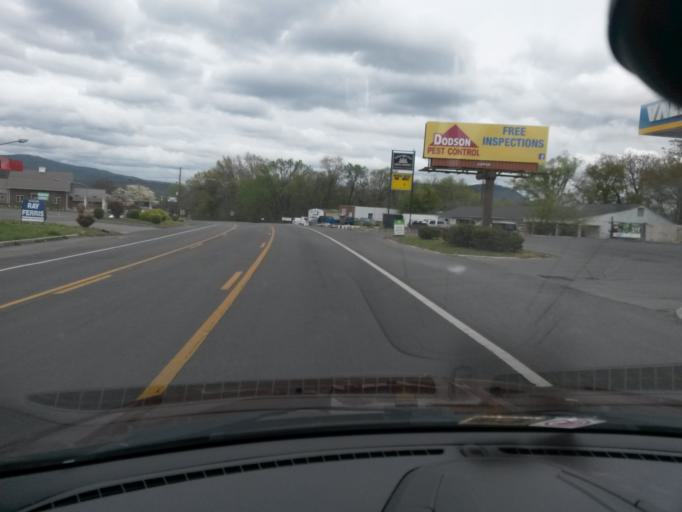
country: US
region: Virginia
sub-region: Roanoke County
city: Hollins
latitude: 37.3268
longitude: -79.9529
